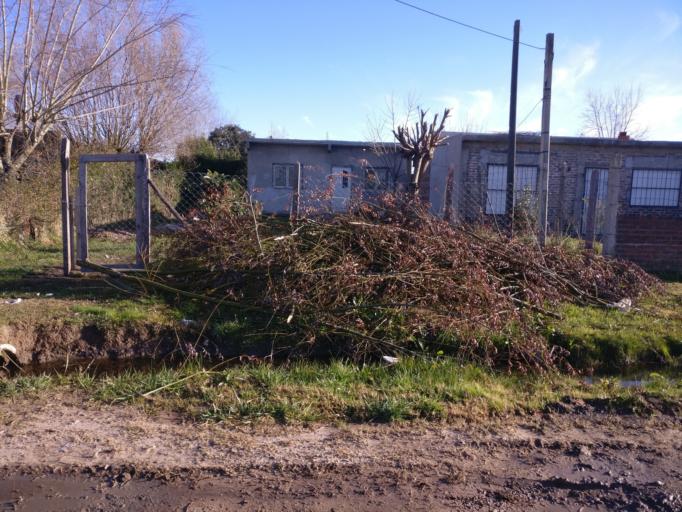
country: AR
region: Buenos Aires
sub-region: Partido de Ezeiza
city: Ezeiza
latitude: -34.9361
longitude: -58.6050
